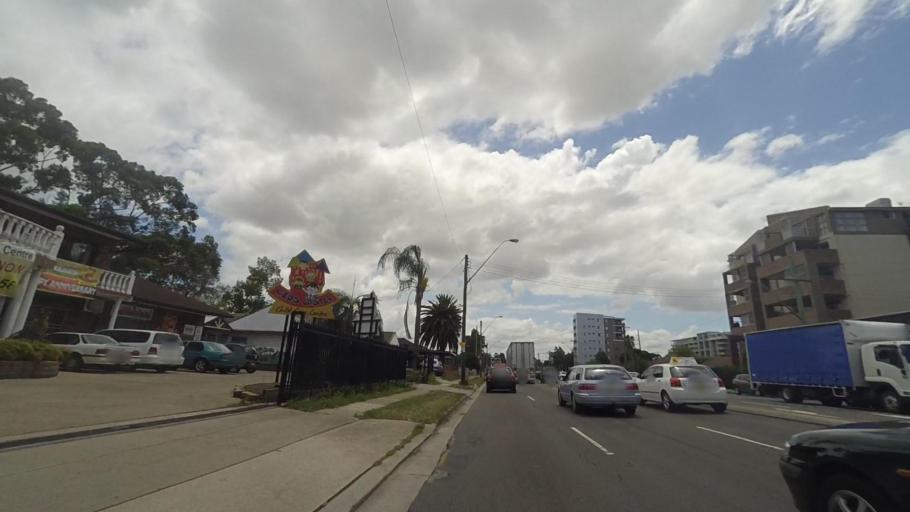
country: AU
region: New South Wales
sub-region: Fairfield
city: Liverpool
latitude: -33.9186
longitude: 150.9195
